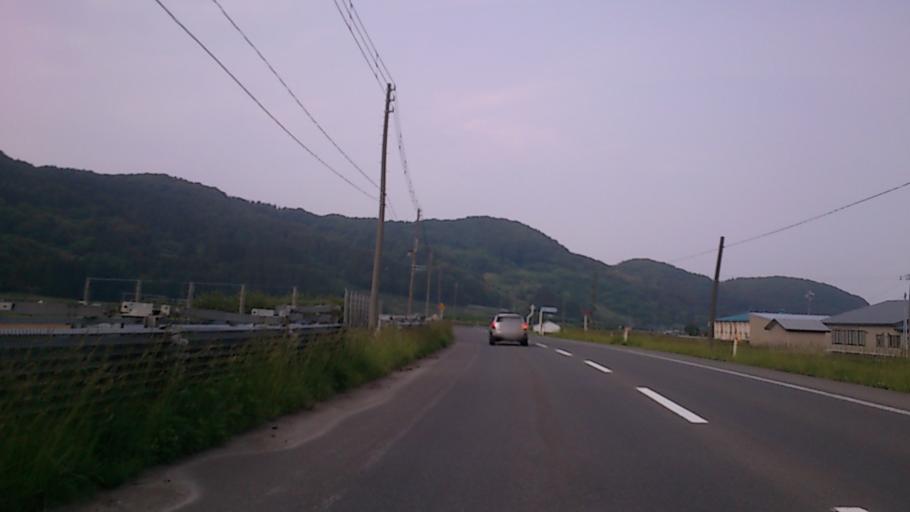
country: JP
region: Aomori
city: Hirosaki
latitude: 40.5850
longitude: 140.3102
